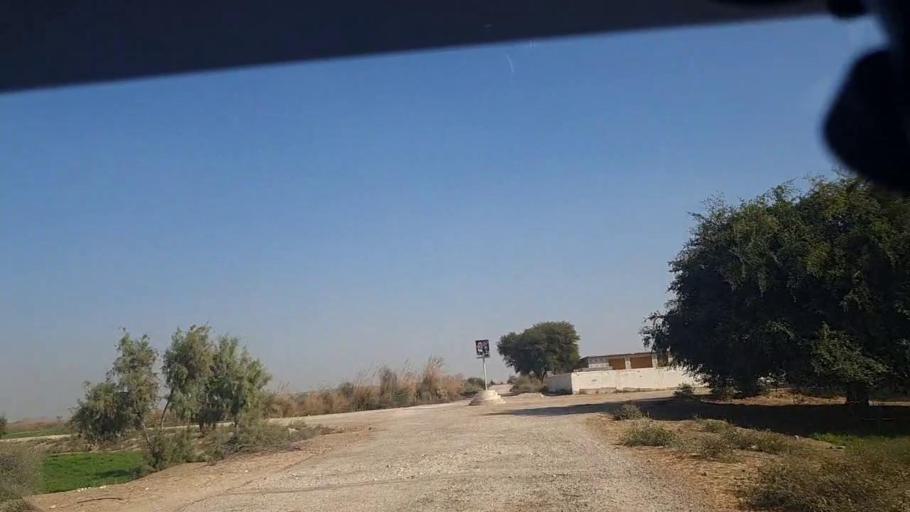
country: PK
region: Sindh
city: Khanpur
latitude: 27.5578
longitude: 69.3340
